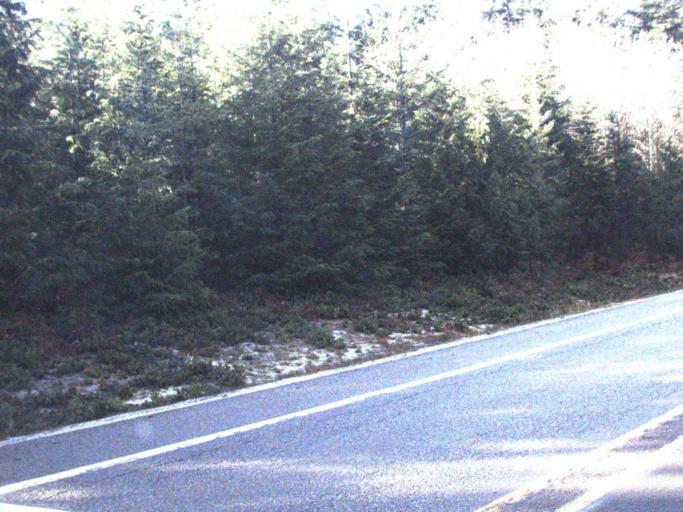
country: US
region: Washington
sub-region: Snohomish County
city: Darrington
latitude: 48.2720
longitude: -121.6474
